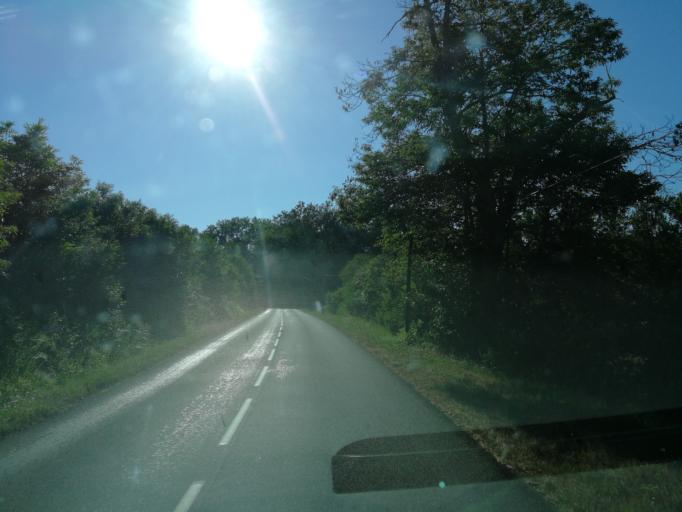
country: FR
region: Midi-Pyrenees
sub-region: Departement du Lot
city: Prayssac
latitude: 44.5966
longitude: 1.1824
